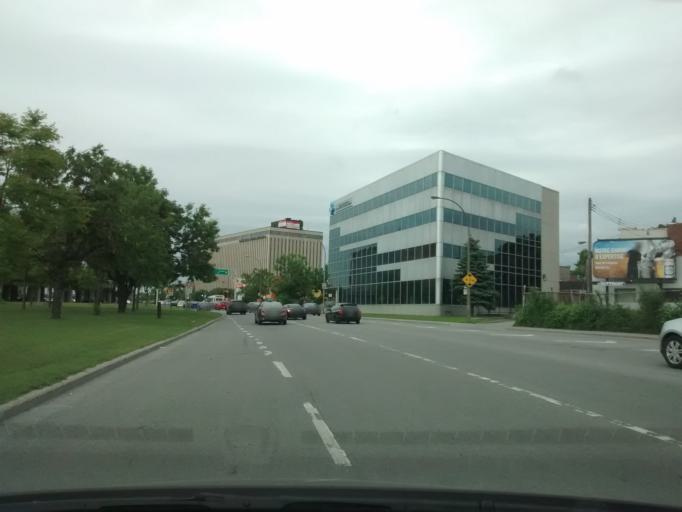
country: CA
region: Quebec
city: Mont-Royal
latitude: 45.5493
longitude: -73.6315
